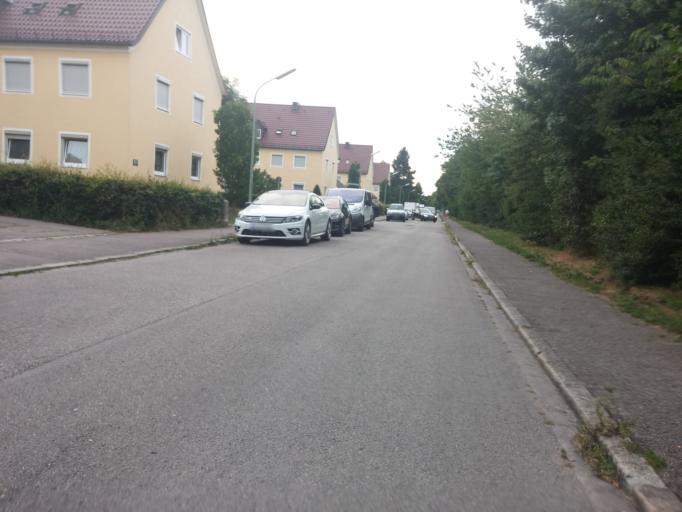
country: DE
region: Bavaria
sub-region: Upper Bavaria
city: Haar
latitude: 48.1163
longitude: 11.6874
